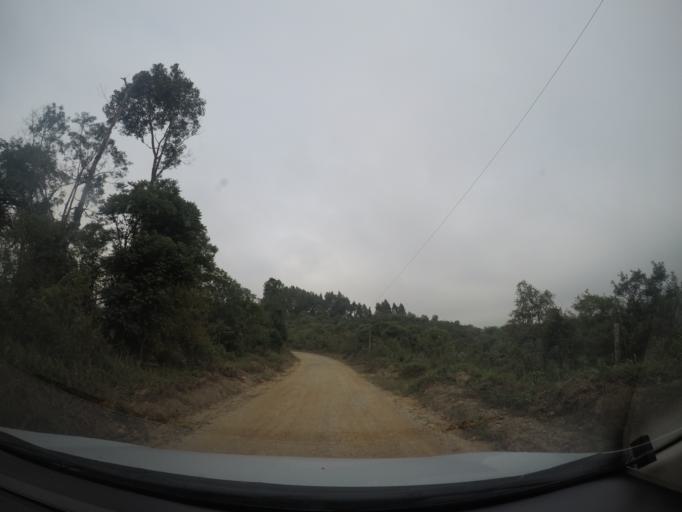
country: BR
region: Parana
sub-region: Colombo
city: Colombo
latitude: -25.3140
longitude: -49.2465
